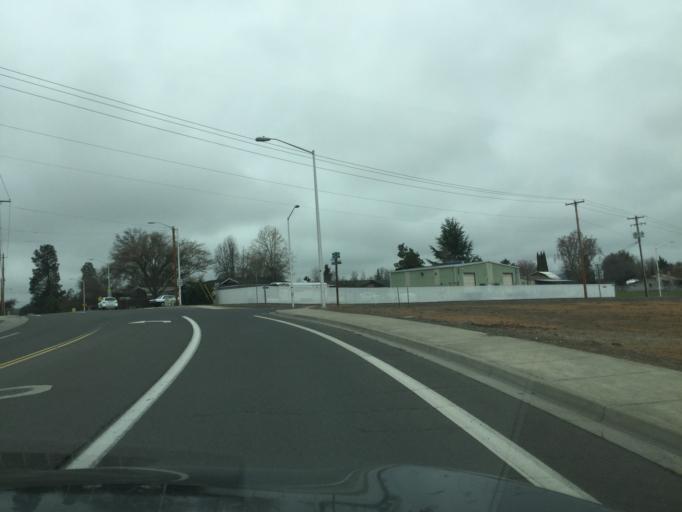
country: US
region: Oregon
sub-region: Jackson County
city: Central Point
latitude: 42.3874
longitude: -122.9202
